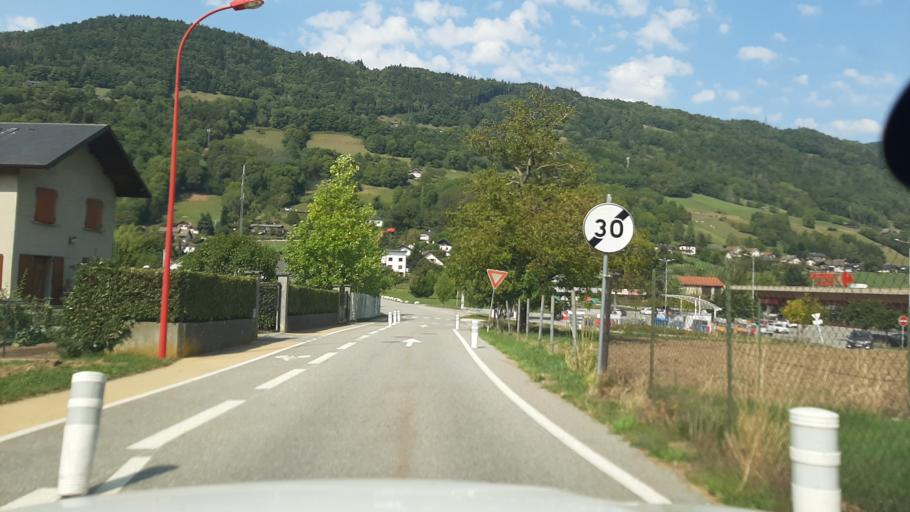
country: FR
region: Rhone-Alpes
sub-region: Departement de la Savoie
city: La Rochette
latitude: 45.4568
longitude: 6.1116
